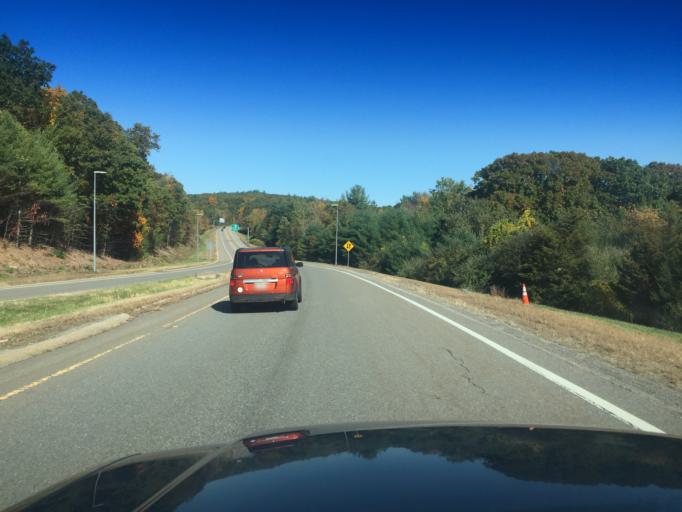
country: US
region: Massachusetts
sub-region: Middlesex County
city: Hudson
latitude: 42.3648
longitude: -71.5814
